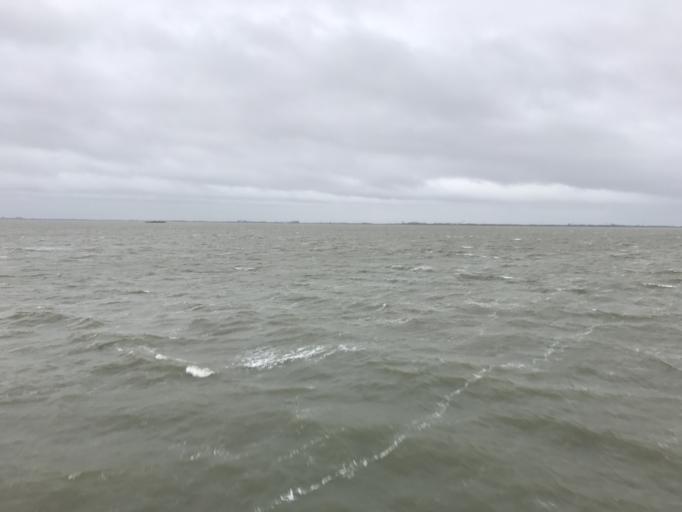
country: NL
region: Groningen
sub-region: Gemeente Delfzijl
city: Delfzijl
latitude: 53.4186
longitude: 6.9318
